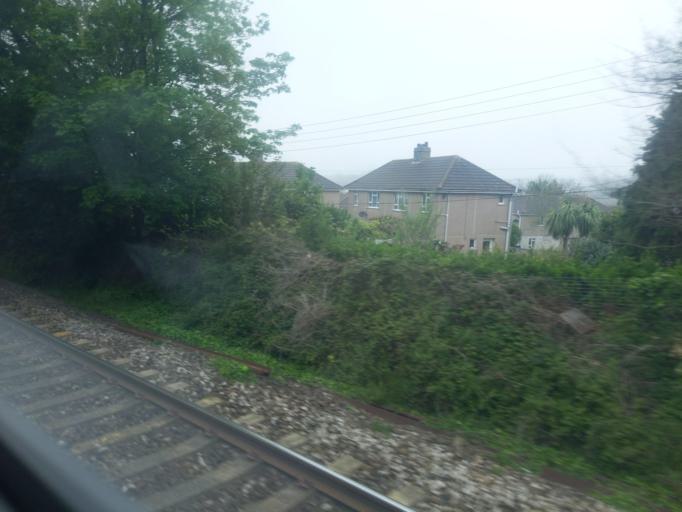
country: GB
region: England
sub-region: Cornwall
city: Hayle
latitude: 50.1880
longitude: -5.4122
